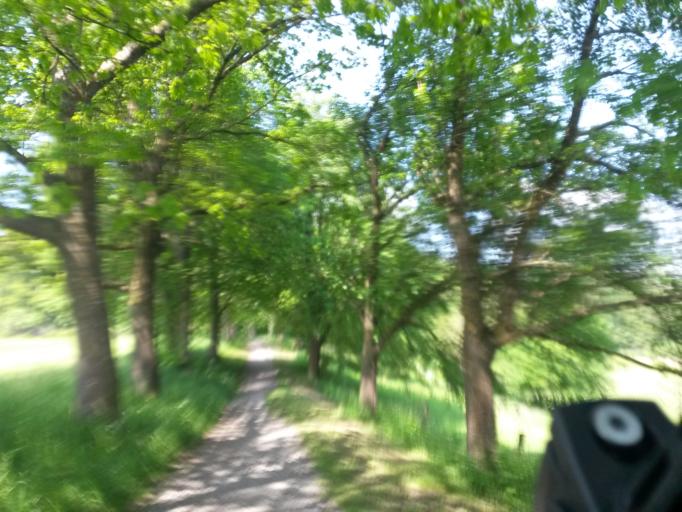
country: DE
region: Baden-Wuerttemberg
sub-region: Tuebingen Region
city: Bad Waldsee
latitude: 47.9088
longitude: 9.7616
